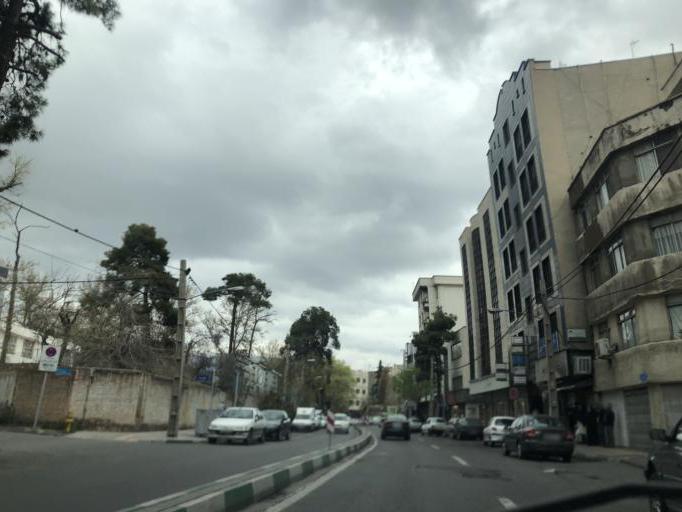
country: IR
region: Tehran
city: Tajrish
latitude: 35.7758
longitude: 51.4376
